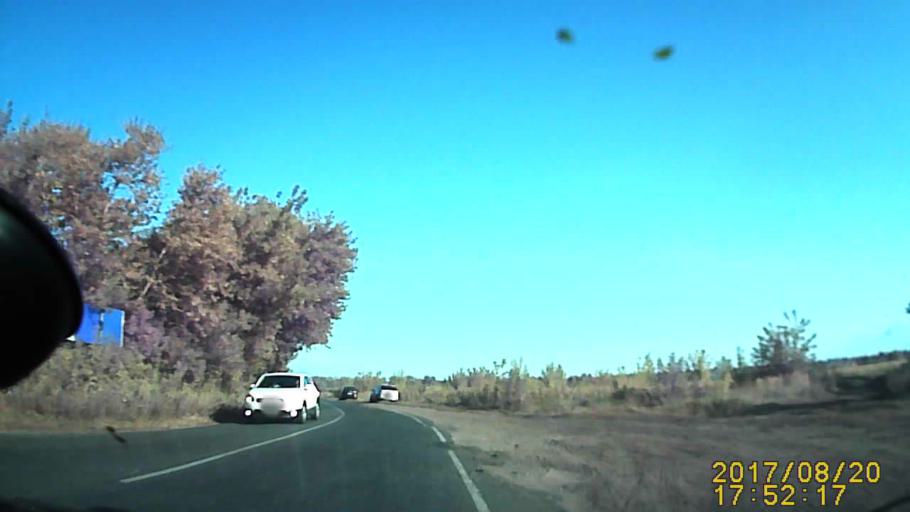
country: RU
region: Ulyanovsk
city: Cherdakly
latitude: 54.4360
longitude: 48.8244
